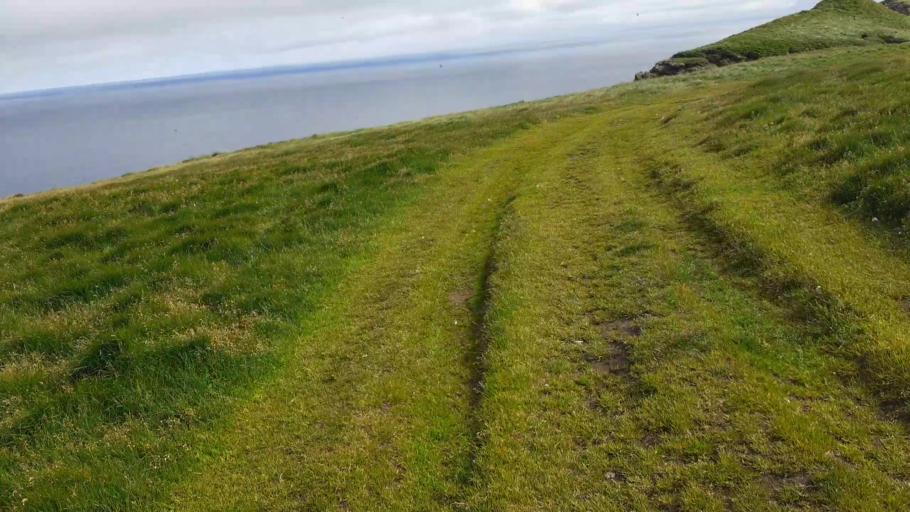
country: IS
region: Northeast
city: Dalvik
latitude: 66.5492
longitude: -17.9922
